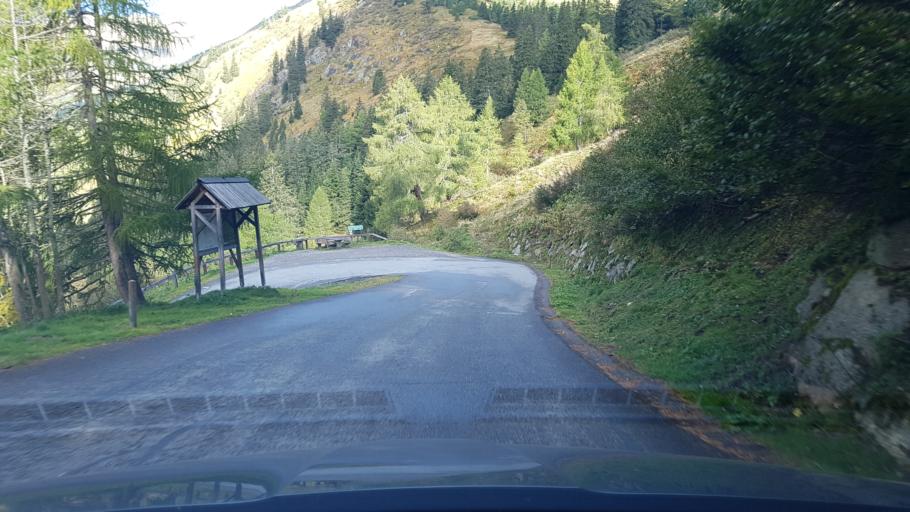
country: AT
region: Styria
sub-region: Politischer Bezirk Liezen
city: Sankt Nikolai im Solktal
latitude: 47.2582
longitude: 14.0813
